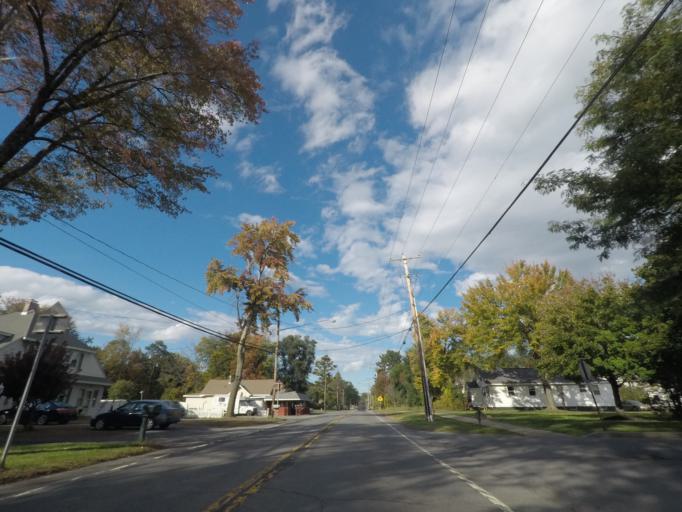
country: US
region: New York
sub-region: Schenectady County
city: Rotterdam
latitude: 42.7427
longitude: -73.9426
